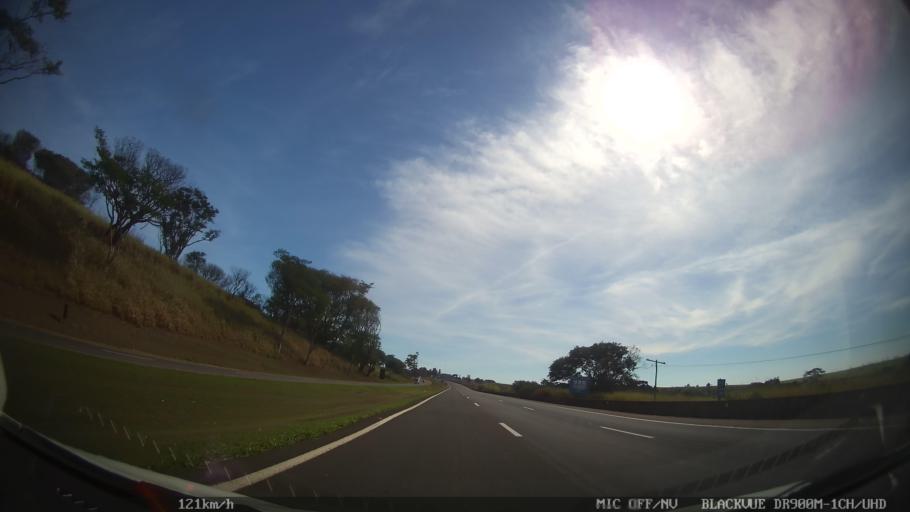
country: BR
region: Sao Paulo
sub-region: Leme
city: Leme
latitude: -22.1574
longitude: -47.3999
